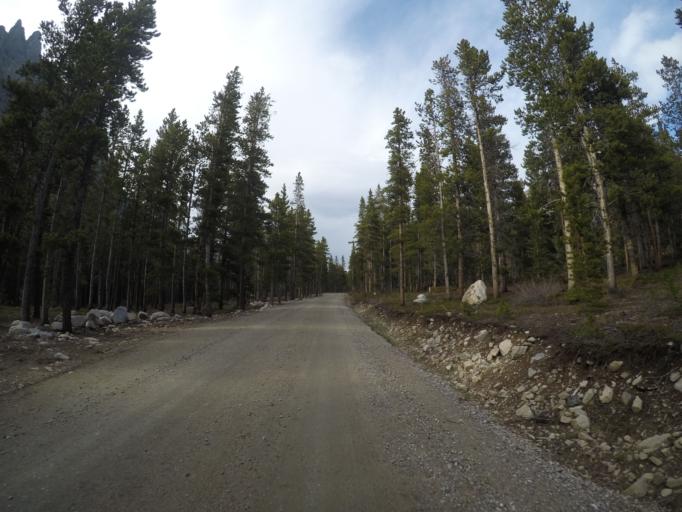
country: US
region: Montana
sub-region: Carbon County
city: Red Lodge
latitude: 45.0311
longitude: -109.4338
